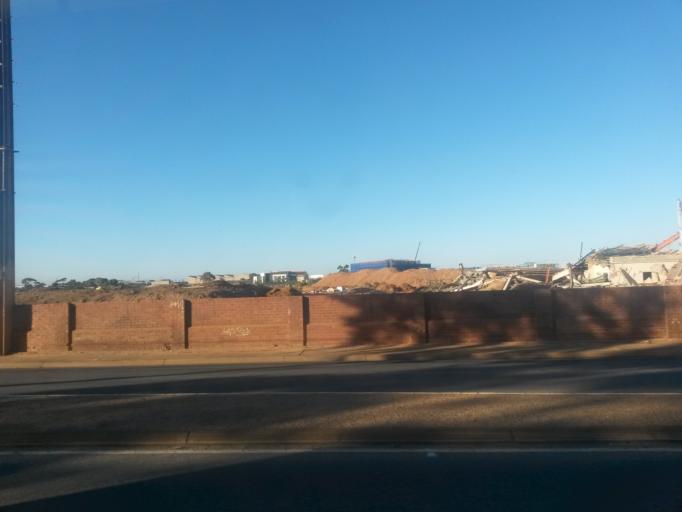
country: AU
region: South Australia
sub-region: Charles Sturt
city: Woodville North
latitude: -34.8660
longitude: 138.5332
